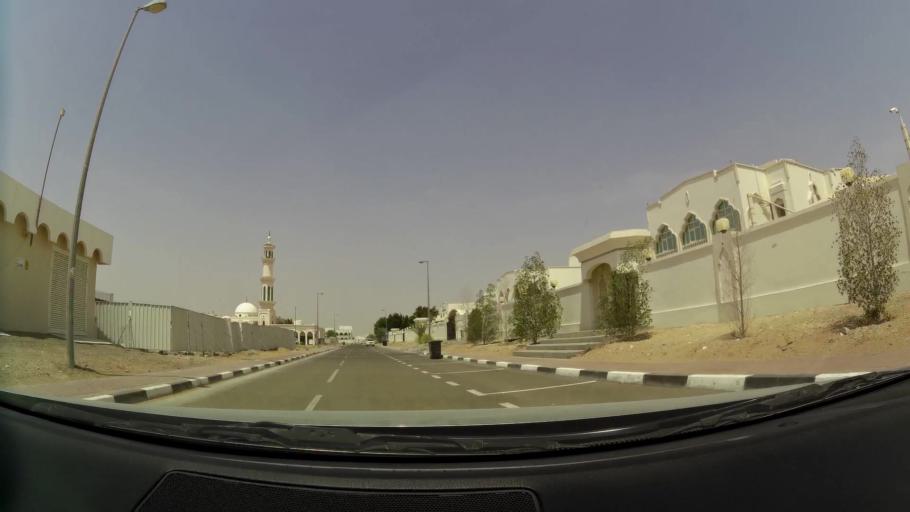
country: AE
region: Abu Dhabi
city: Al Ain
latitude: 24.1895
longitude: 55.7286
